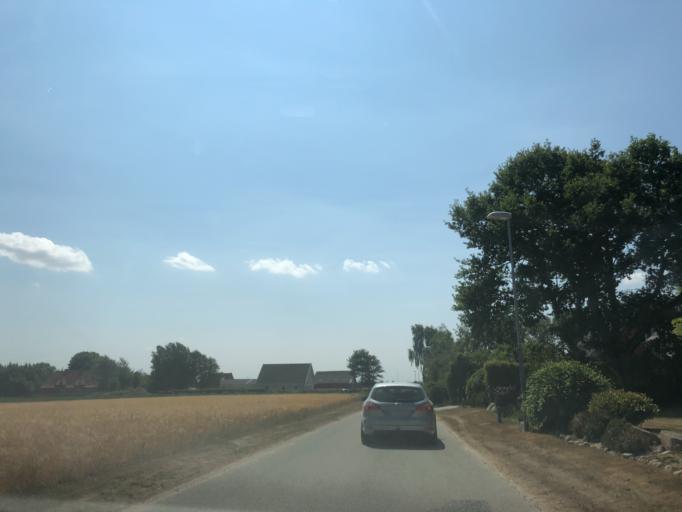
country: DK
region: North Denmark
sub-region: Morso Kommune
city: Nykobing Mors
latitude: 56.8244
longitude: 8.9965
